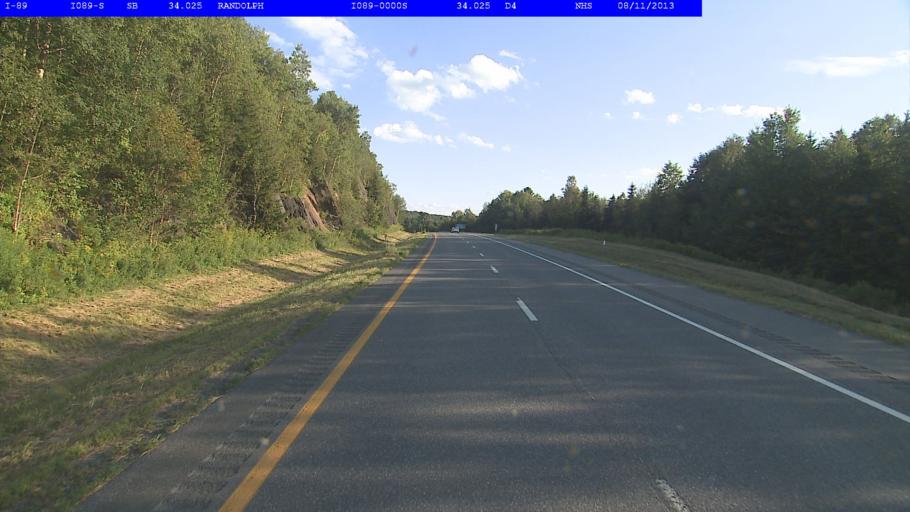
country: US
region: Vermont
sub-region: Orange County
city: Randolph
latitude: 43.9901
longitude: -72.6276
